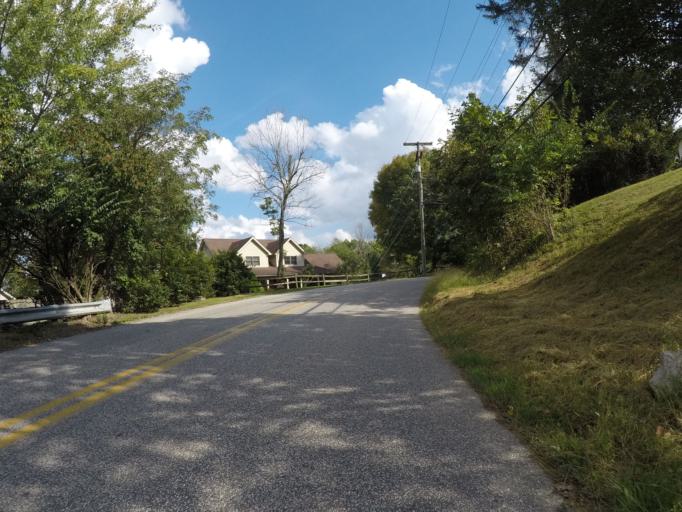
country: US
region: West Virginia
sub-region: Cabell County
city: Huntington
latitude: 38.3984
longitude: -82.4344
